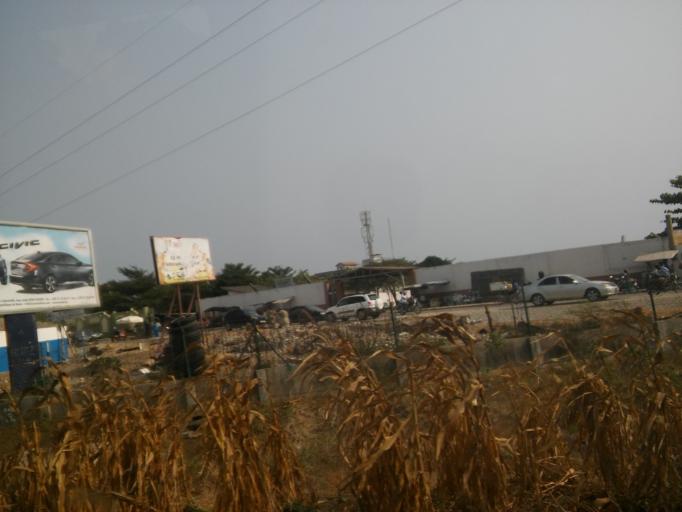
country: BJ
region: Littoral
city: Cotonou
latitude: 6.3720
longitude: 2.5377
